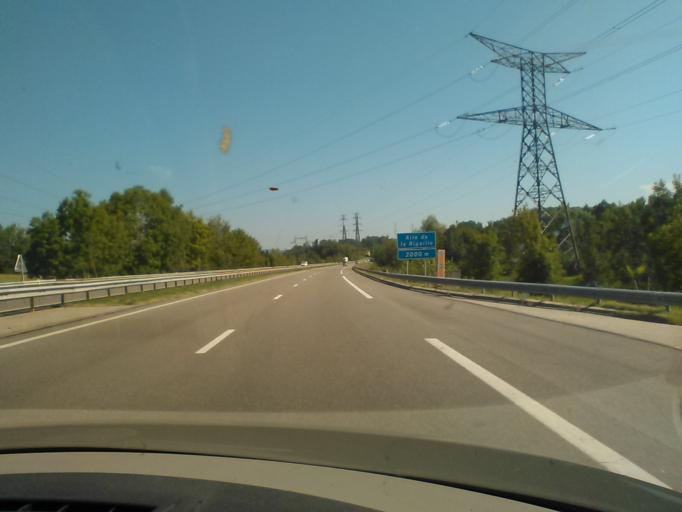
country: FR
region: Rhone-Alpes
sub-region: Departement de la Haute-Savoie
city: Chavanod
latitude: 45.8612
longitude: 6.0570
